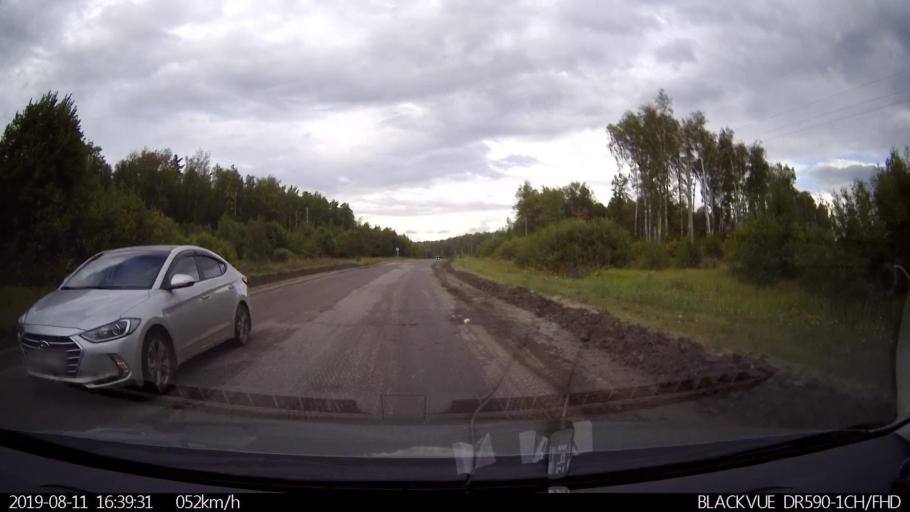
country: RU
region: Ulyanovsk
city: Mayna
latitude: 54.1403
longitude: 47.6378
